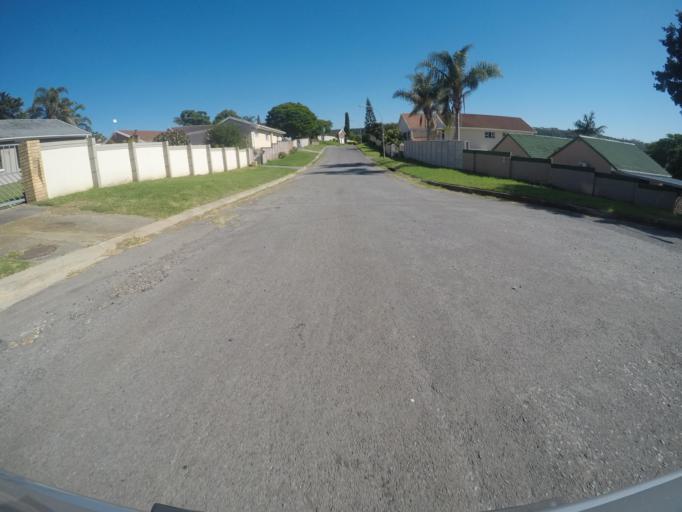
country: ZA
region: Eastern Cape
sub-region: Buffalo City Metropolitan Municipality
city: East London
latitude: -32.9485
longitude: 27.9002
